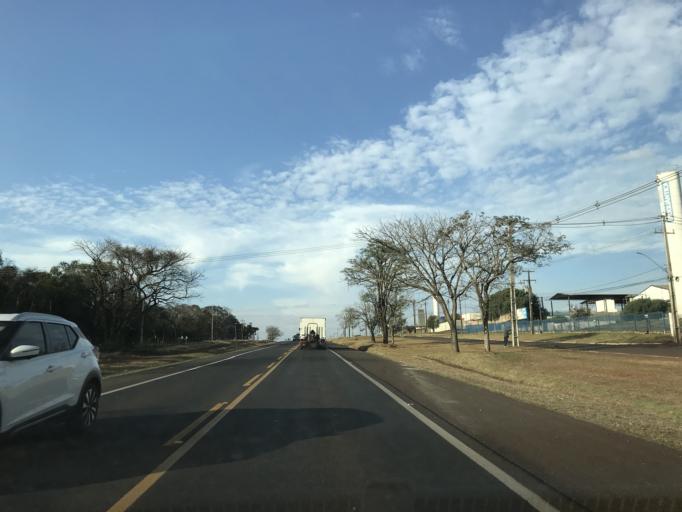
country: BR
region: Parana
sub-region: Cascavel
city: Cascavel
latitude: -25.0397
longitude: -53.5993
